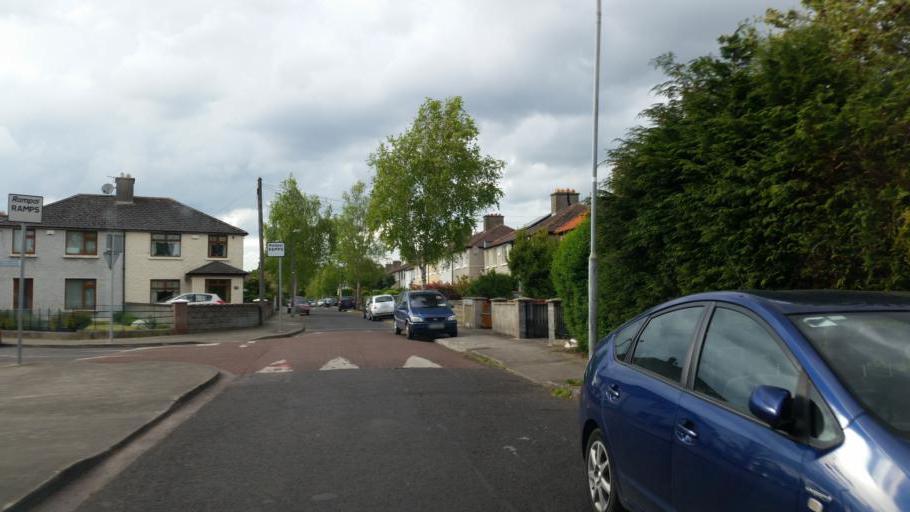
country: IE
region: Leinster
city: Marino
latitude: 53.3688
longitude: -6.2325
